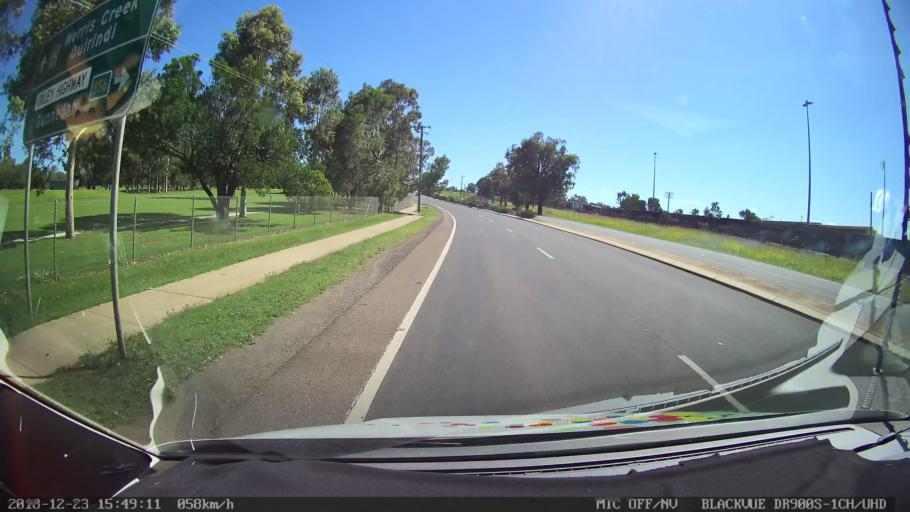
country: AU
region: New South Wales
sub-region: Tamworth Municipality
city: South Tamworth
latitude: -31.0974
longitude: 150.9084
